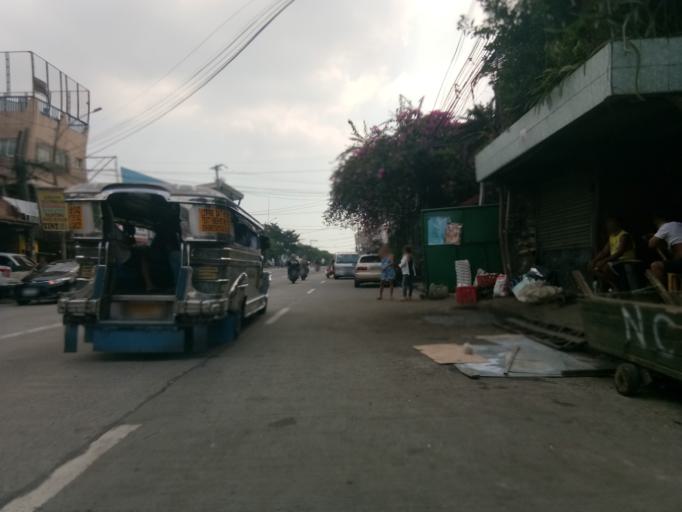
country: PH
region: Metro Manila
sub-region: Marikina
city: Calumpang
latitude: 14.6185
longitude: 121.0641
